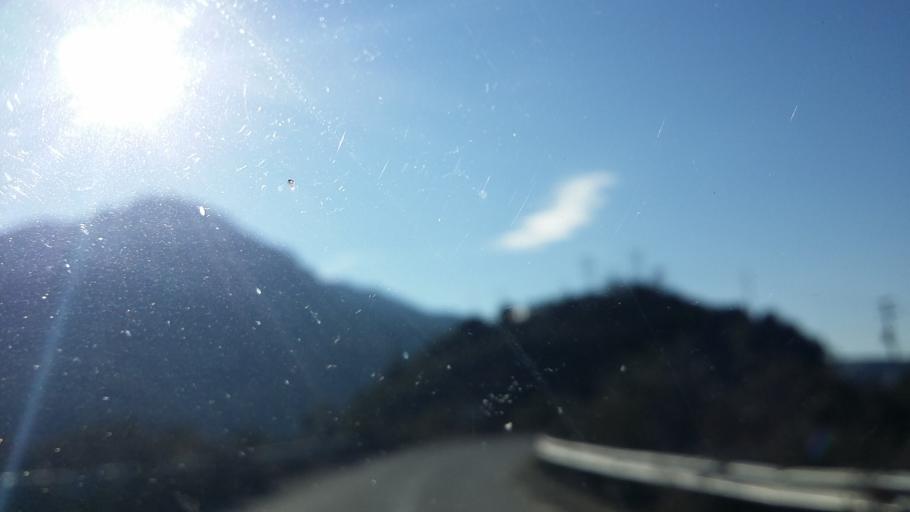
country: GR
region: Central Greece
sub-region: Nomos Evrytanias
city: Kerasochori
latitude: 38.8878
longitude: 21.6076
